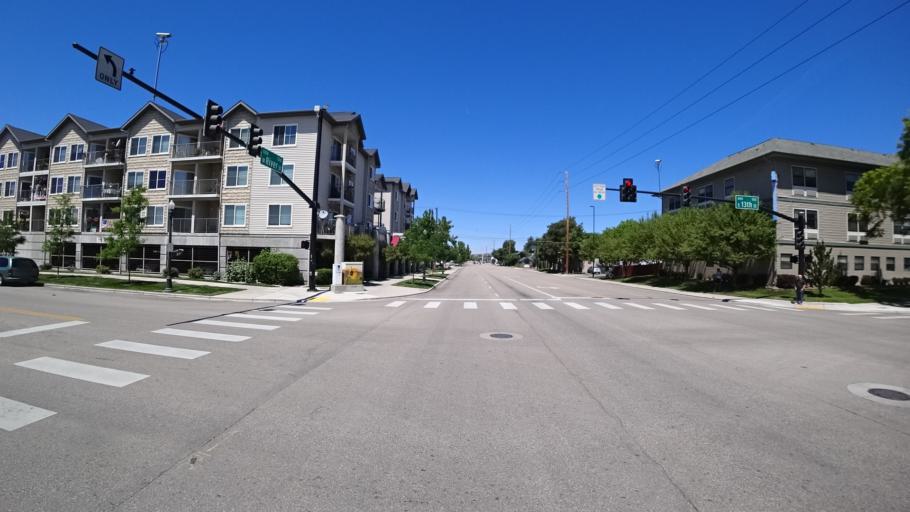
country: US
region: Idaho
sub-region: Ada County
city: Boise
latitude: 43.6150
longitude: -116.2149
